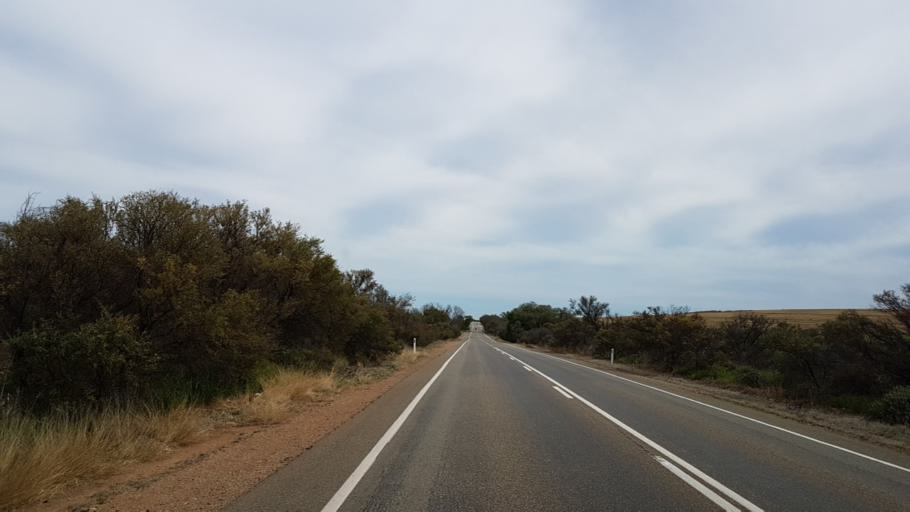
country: AU
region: South Australia
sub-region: Port Pirie City and Dists
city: Crystal Brook
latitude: -33.2360
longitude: 138.3891
